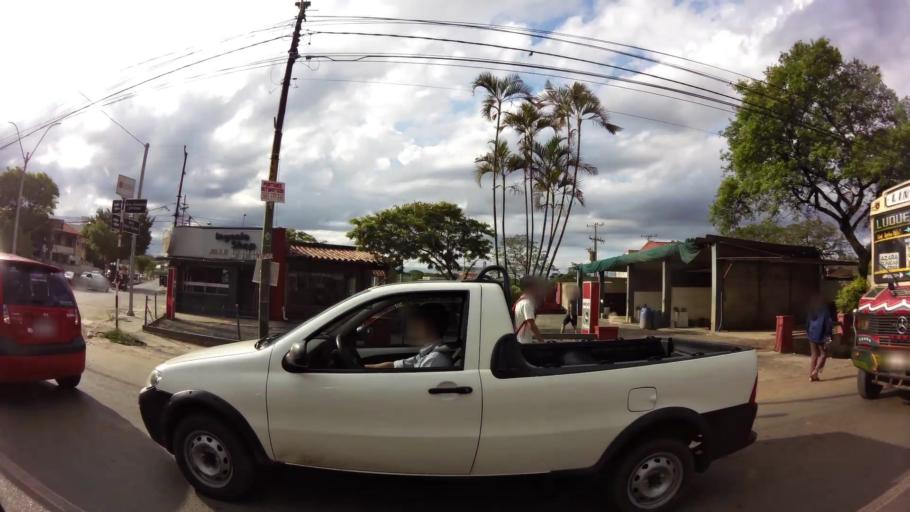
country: PY
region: Central
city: Fernando de la Mora
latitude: -25.2771
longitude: -57.5517
